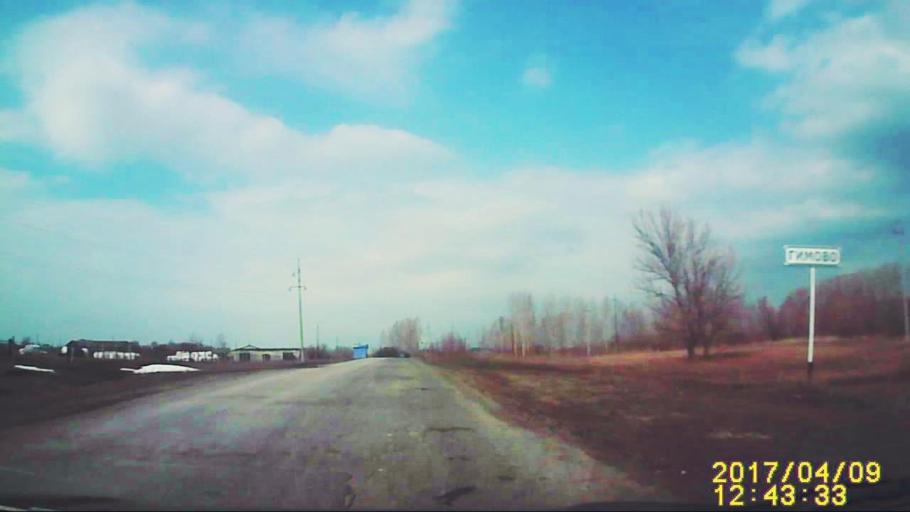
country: RU
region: Ulyanovsk
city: Ignatovka
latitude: 54.0082
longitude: 47.9175
